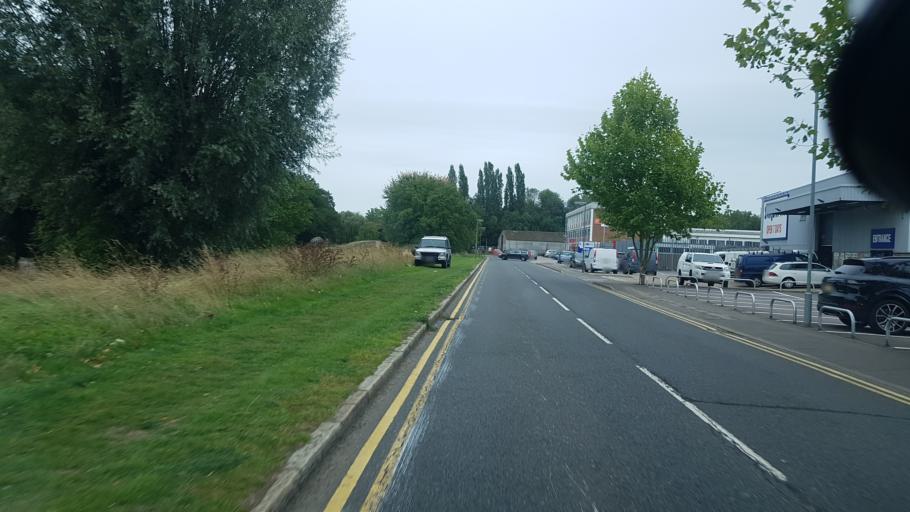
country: GB
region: England
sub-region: Surrey
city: Guildford
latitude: 51.2468
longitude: -0.5818
